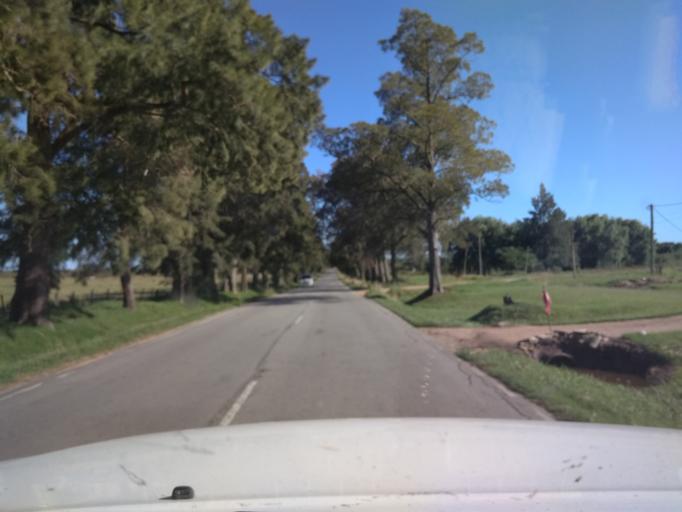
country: UY
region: Canelones
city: San Bautista
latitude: -34.3901
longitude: -55.9595
